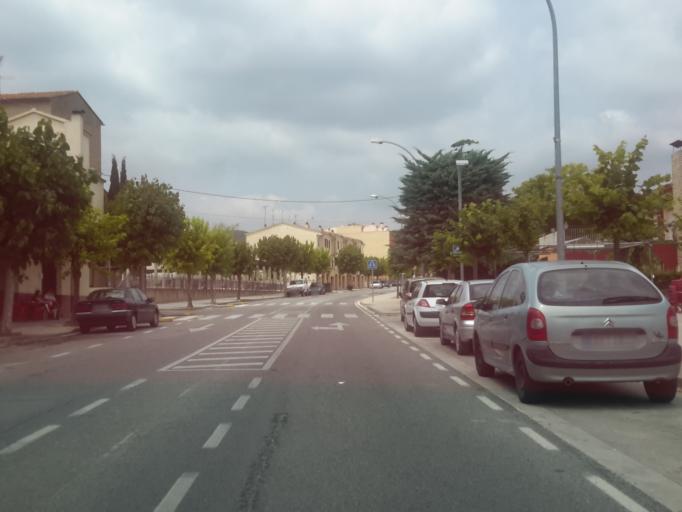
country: ES
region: Catalonia
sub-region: Provincia de Barcelona
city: Sant Marti Sarroca
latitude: 41.3873
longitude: 1.5732
